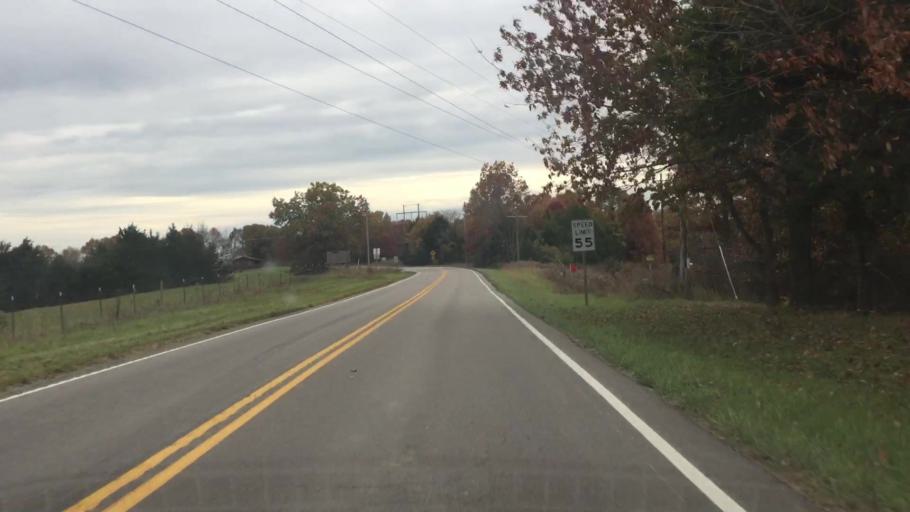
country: US
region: Missouri
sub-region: Gasconade County
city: Hermann
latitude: 38.7233
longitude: -91.7057
